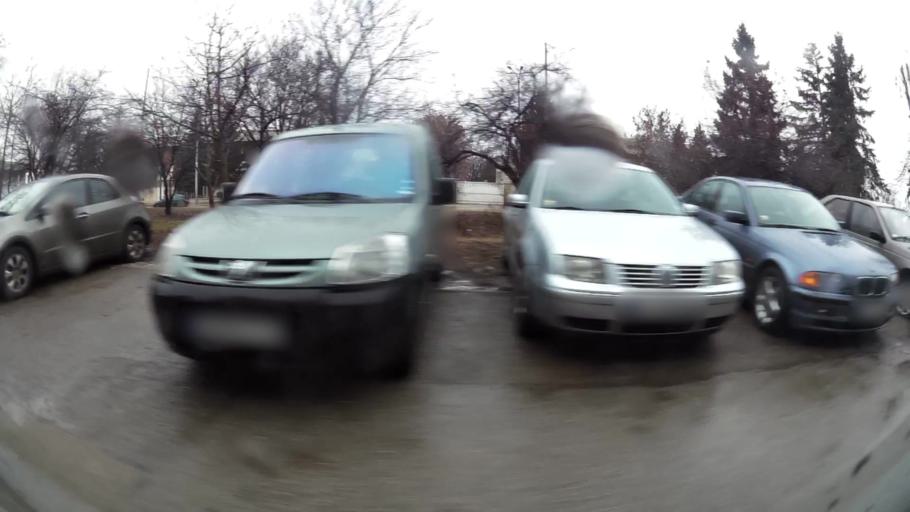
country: BG
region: Sofia-Capital
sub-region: Stolichna Obshtina
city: Sofia
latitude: 42.6540
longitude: 23.3686
